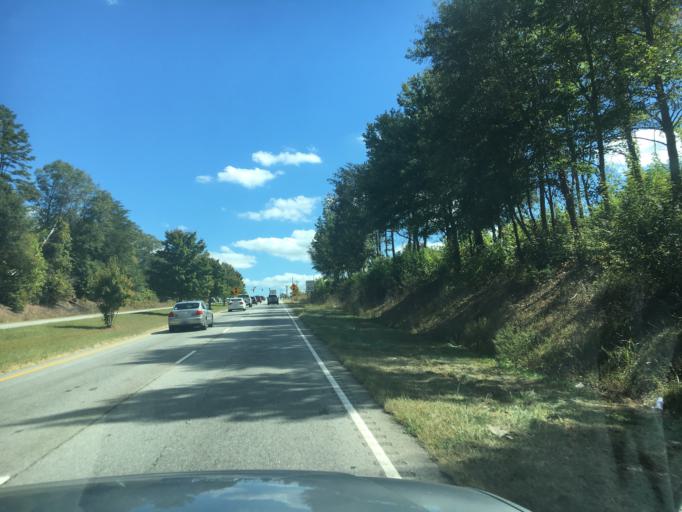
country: US
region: South Carolina
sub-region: Spartanburg County
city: Fairforest
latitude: 34.9389
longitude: -82.0378
